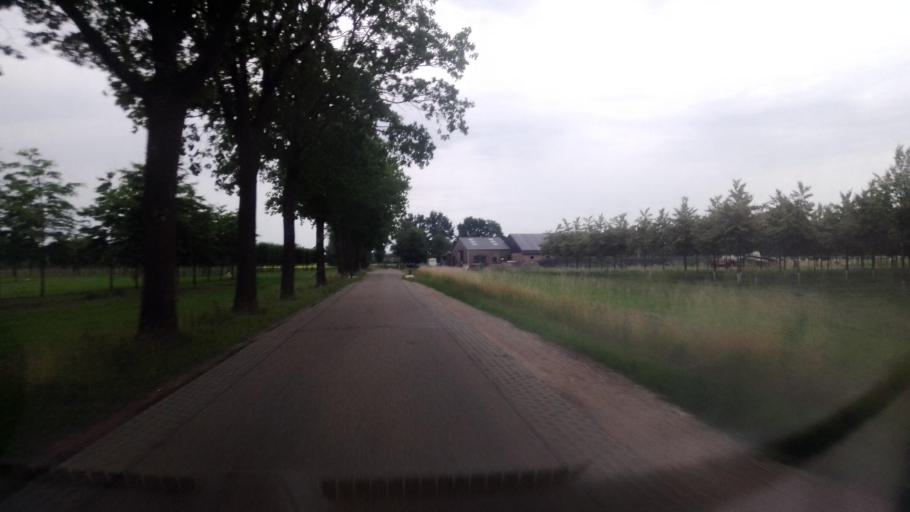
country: NL
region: Limburg
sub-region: Gemeente Beesel
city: Offenbeek
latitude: 51.2835
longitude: 6.1185
